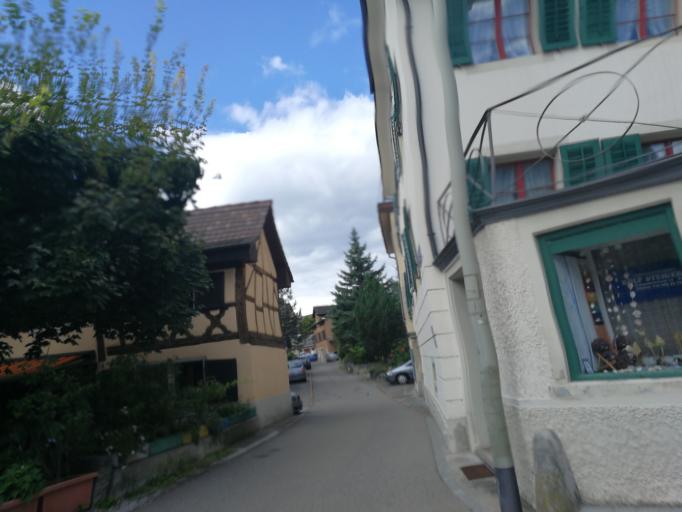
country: CH
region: Zurich
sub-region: Bezirk Meilen
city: Stafa
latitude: 47.2424
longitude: 8.7215
